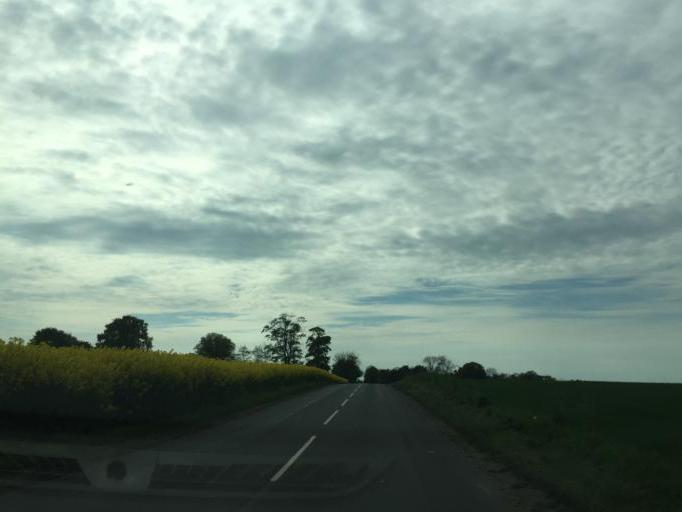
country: DK
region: South Denmark
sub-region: Odense Kommune
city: Hojby
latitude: 55.3399
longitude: 10.4648
